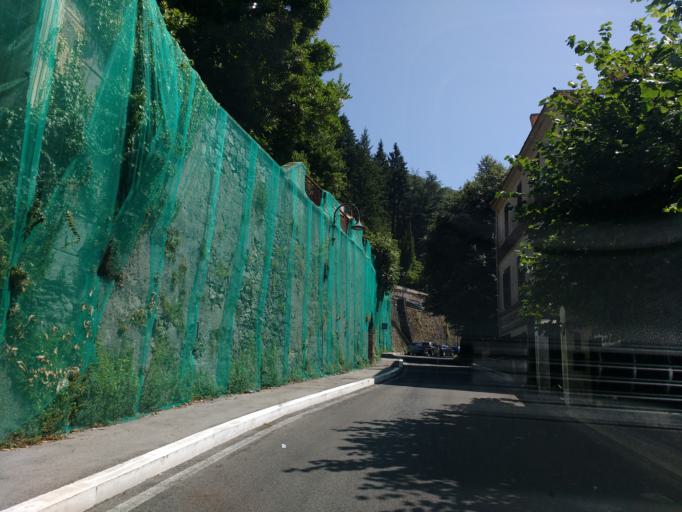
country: IT
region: Latium
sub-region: Citta metropolitana di Roma Capitale
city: Rocca di Papa
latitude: 41.7577
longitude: 12.7074
